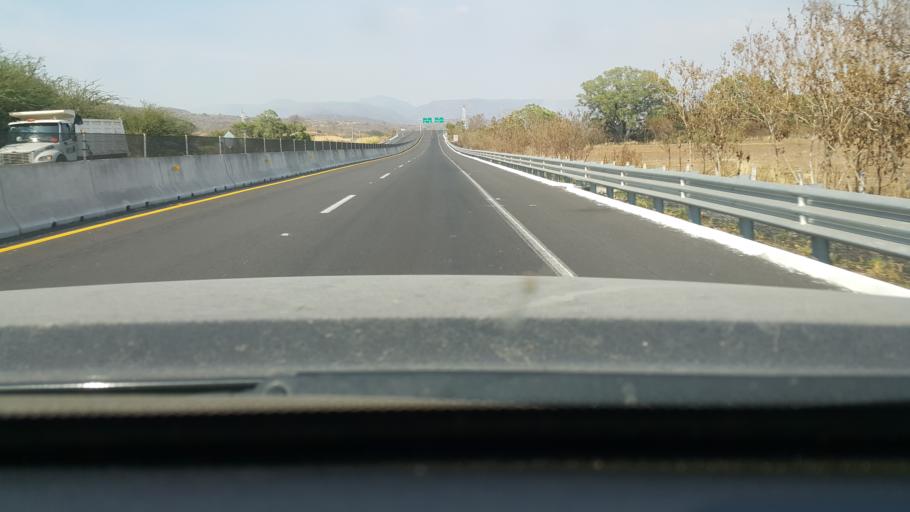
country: MX
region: Nayarit
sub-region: Ahuacatlan
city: Ahuacatlan
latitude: 21.0573
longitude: -104.5136
